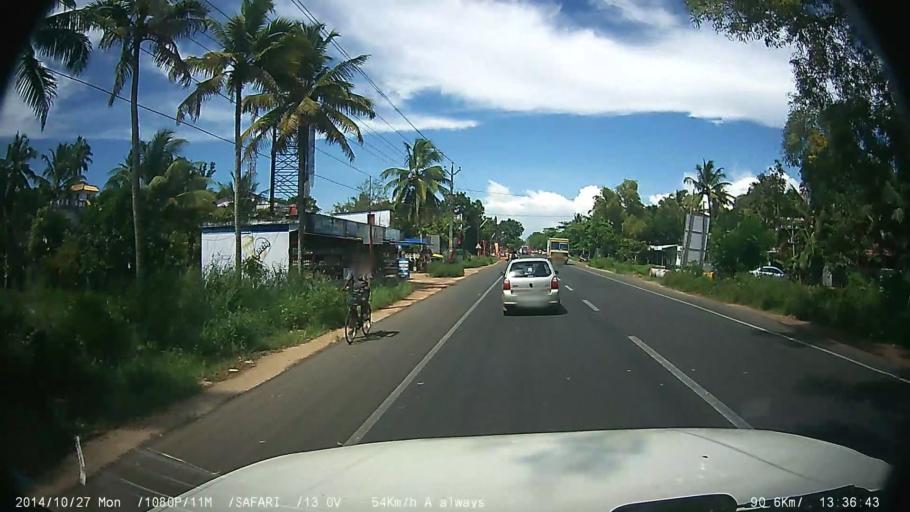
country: IN
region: Kerala
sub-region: Alappuzha
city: Shertallai
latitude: 9.6050
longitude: 76.3289
